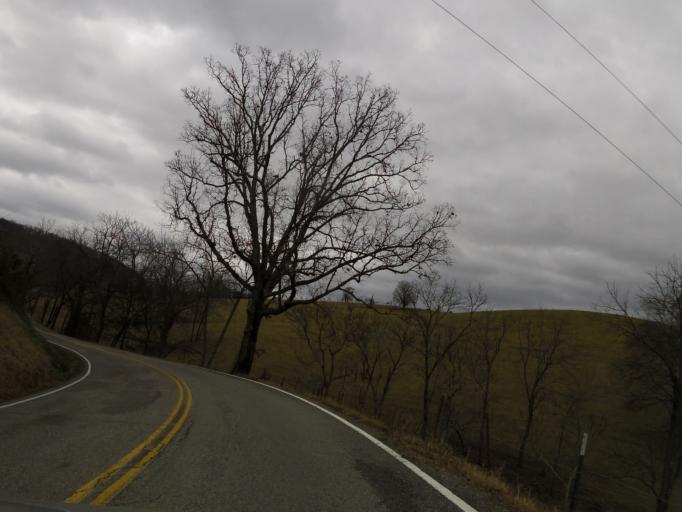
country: US
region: Tennessee
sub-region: Jefferson County
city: Jefferson City
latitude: 36.1834
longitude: -83.5307
